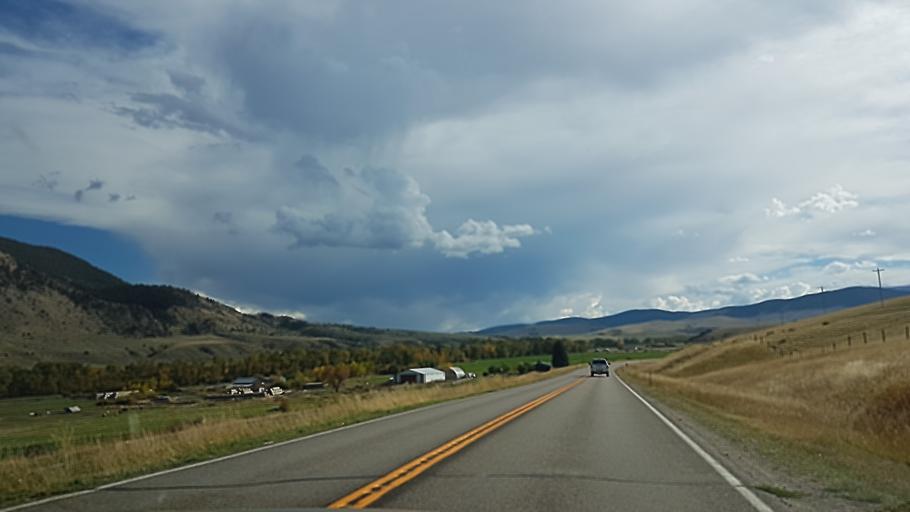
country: US
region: Montana
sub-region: Jefferson County
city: Whitehall
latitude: 45.8238
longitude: -111.9336
